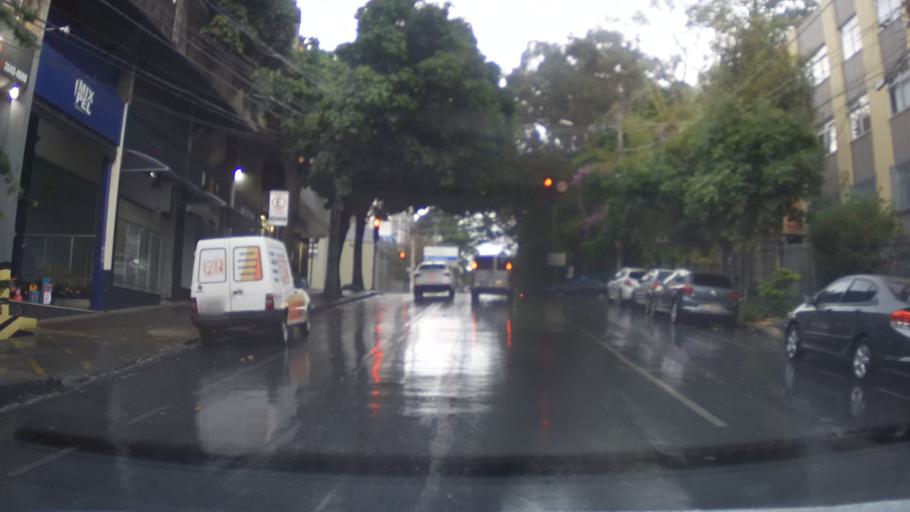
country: BR
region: Minas Gerais
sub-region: Belo Horizonte
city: Belo Horizonte
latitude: -19.9311
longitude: -43.9515
